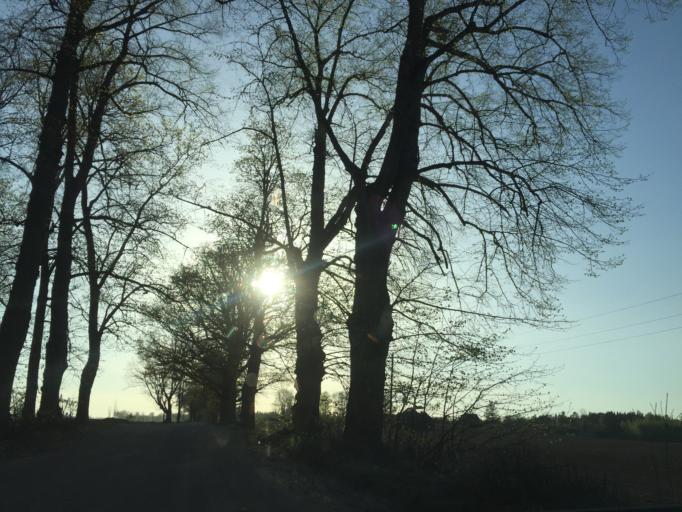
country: LV
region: Ergli
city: Ergli
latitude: 56.7383
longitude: 25.5954
